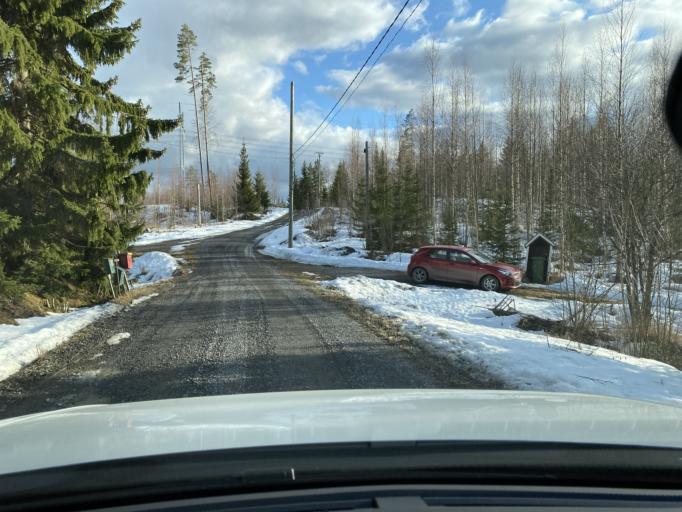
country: FI
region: Pirkanmaa
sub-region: Lounais-Pirkanmaa
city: Mouhijaervi
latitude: 61.4459
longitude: 22.9602
